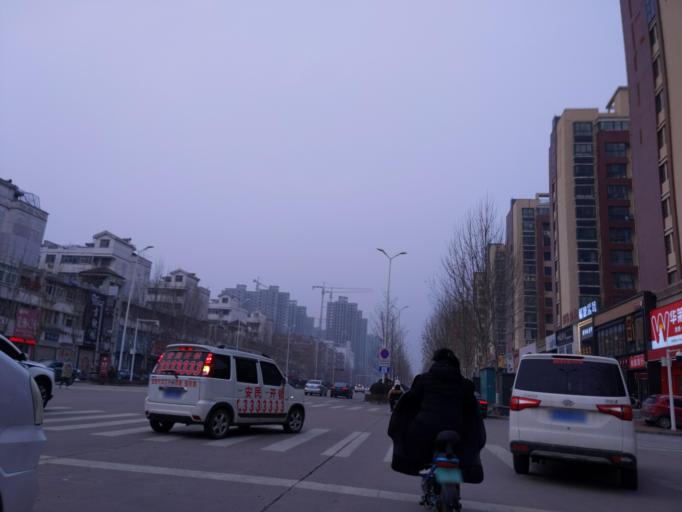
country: CN
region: Henan Sheng
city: Puyang
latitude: 35.7826
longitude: 115.0267
